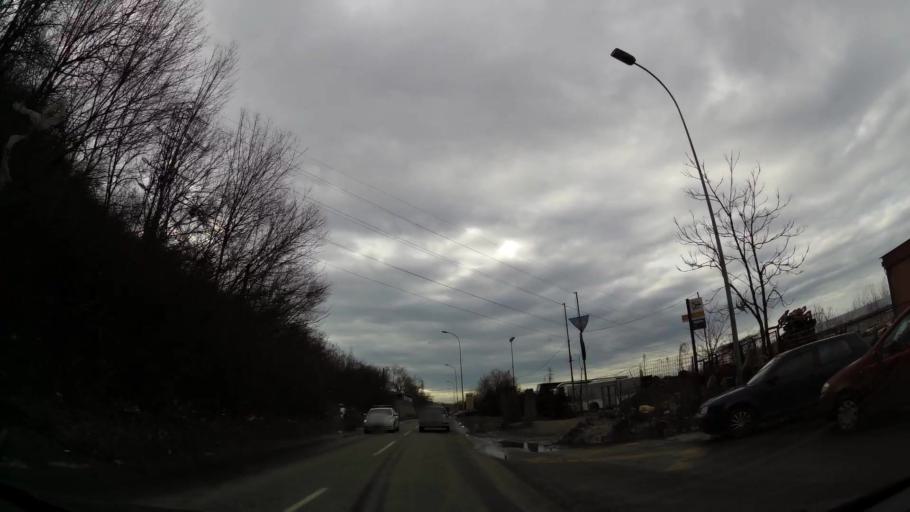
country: RS
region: Central Serbia
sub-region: Belgrade
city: Cukarica
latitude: 44.7691
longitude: 20.4075
